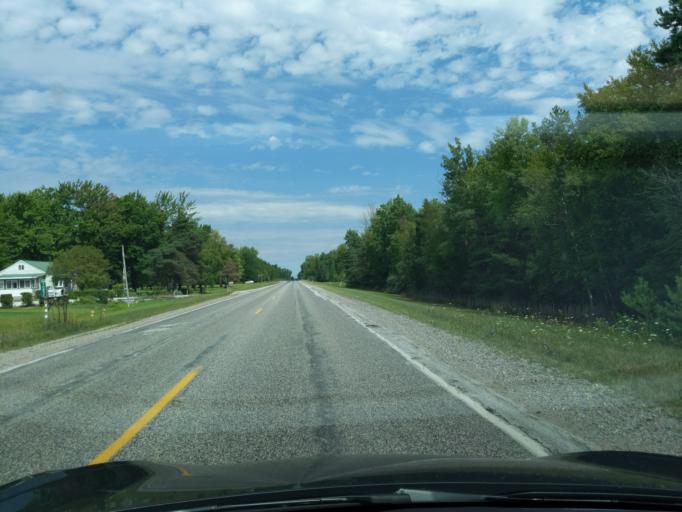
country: US
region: Michigan
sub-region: Gratiot County
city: Breckenridge
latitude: 43.4488
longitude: -84.3700
